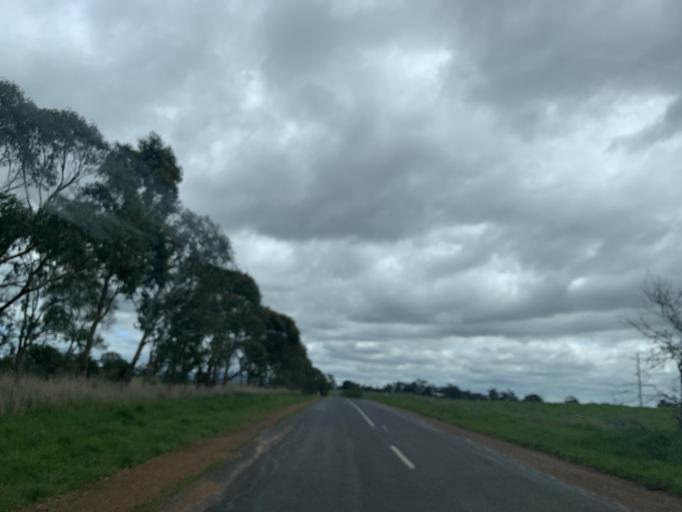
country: AU
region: Victoria
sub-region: Whittlesea
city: Whittlesea
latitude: -37.1859
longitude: 145.0353
